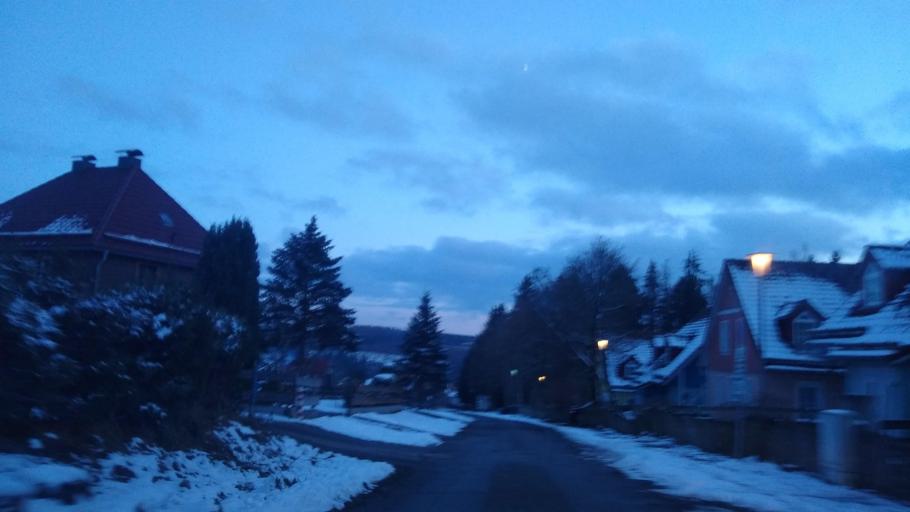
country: DE
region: Saxony-Anhalt
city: Benneckenstein
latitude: 51.7015
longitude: 10.7150
